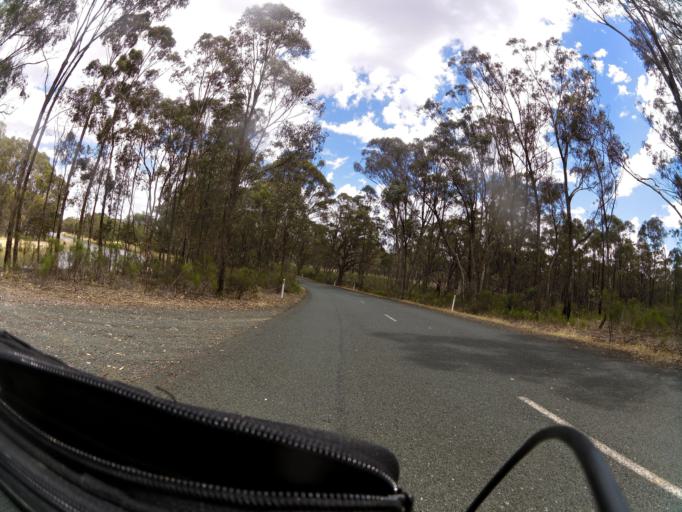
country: AU
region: Victoria
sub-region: Greater Shepparton
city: Shepparton
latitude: -36.6849
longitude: 145.1823
